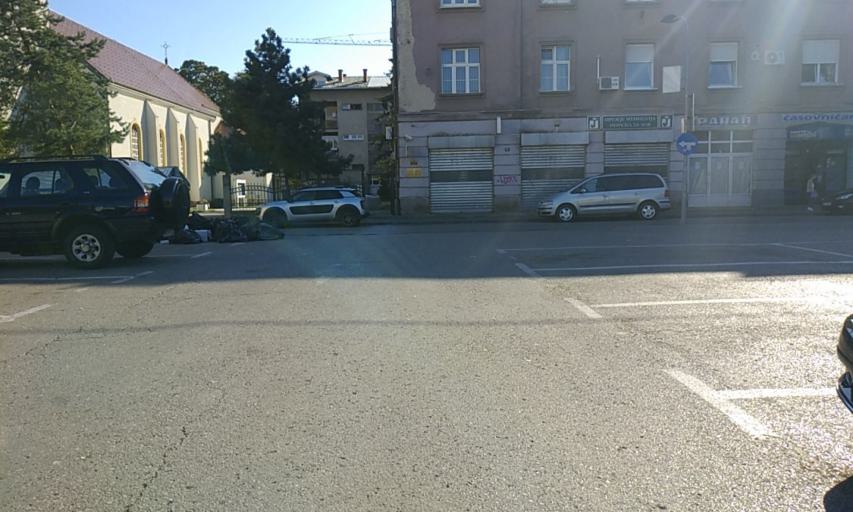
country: BA
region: Republika Srpska
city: Mejdan - Obilicevo
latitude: 44.7715
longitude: 17.1932
